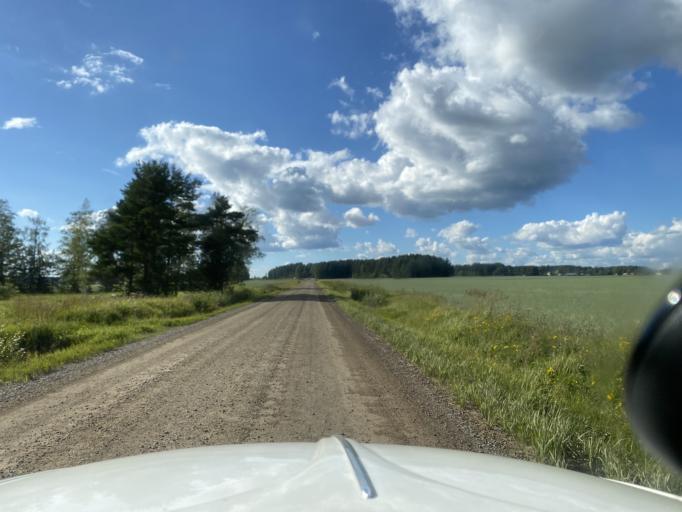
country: FI
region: Pirkanmaa
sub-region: Lounais-Pirkanmaa
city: Punkalaidun
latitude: 61.1344
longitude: 23.2286
